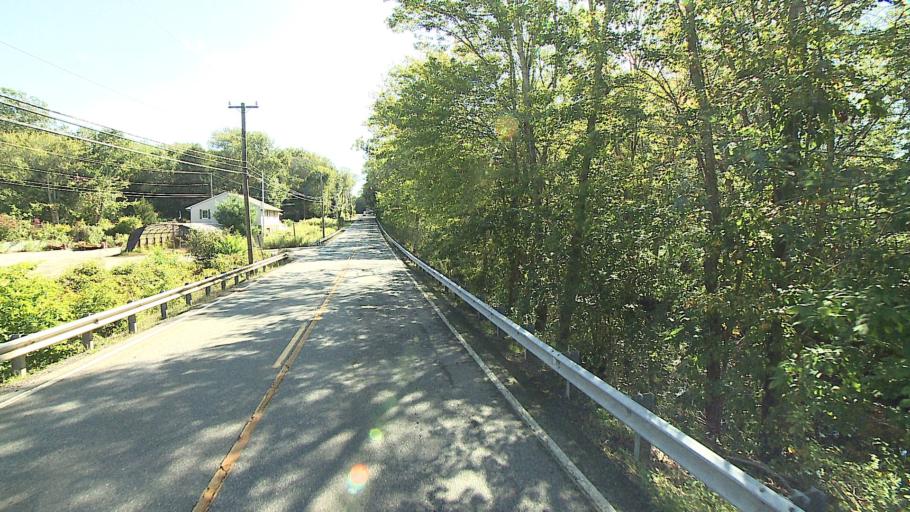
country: US
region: Connecticut
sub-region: New London County
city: Lisbon
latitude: 41.5561
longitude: -72.0274
